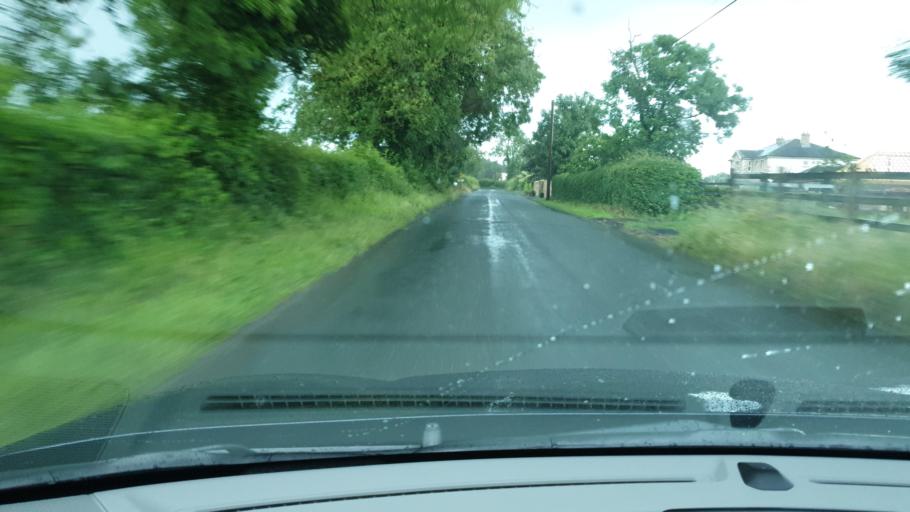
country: IE
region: Leinster
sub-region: An Mhi
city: Navan
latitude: 53.6284
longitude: -6.6866
